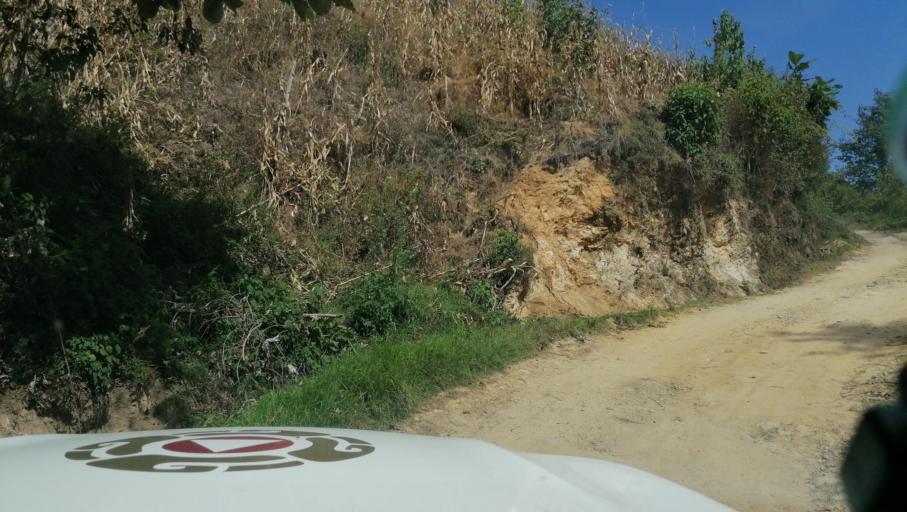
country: GT
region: San Marcos
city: Tacana
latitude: 15.2089
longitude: -92.2157
